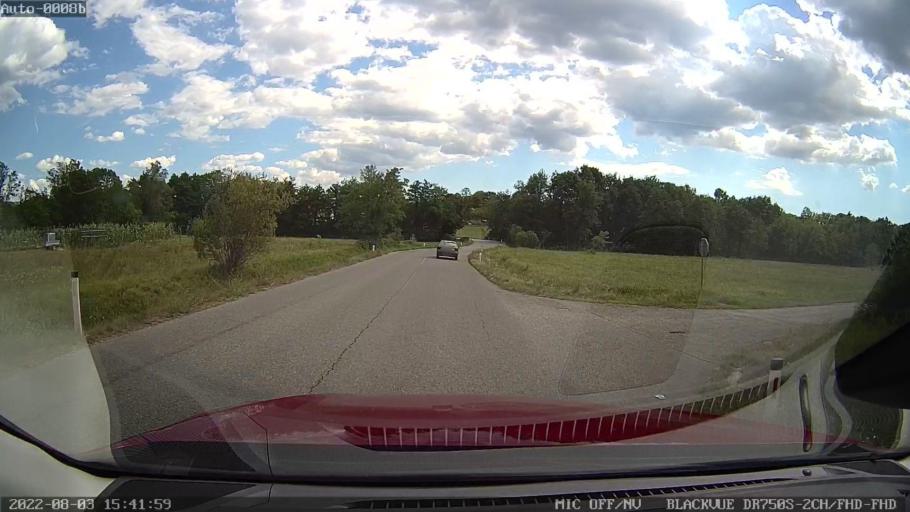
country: SI
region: Sempeter-Vrtojba
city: Rozna Dolina
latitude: 45.9521
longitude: 13.6930
